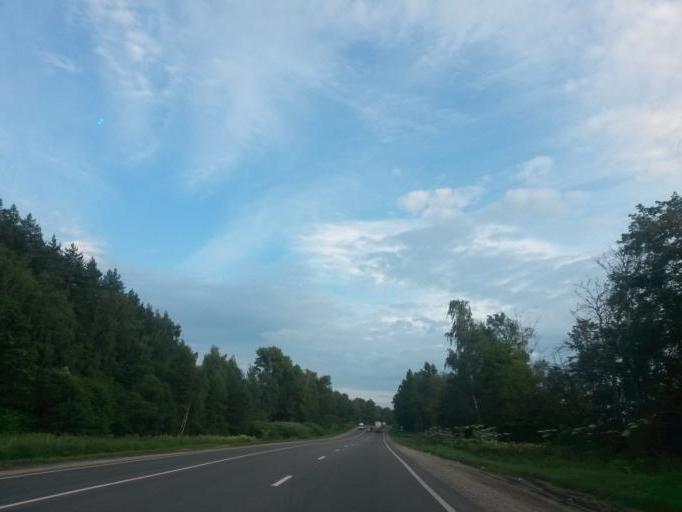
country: RU
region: Moskovskaya
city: Barybino
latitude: 55.2307
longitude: 37.8663
